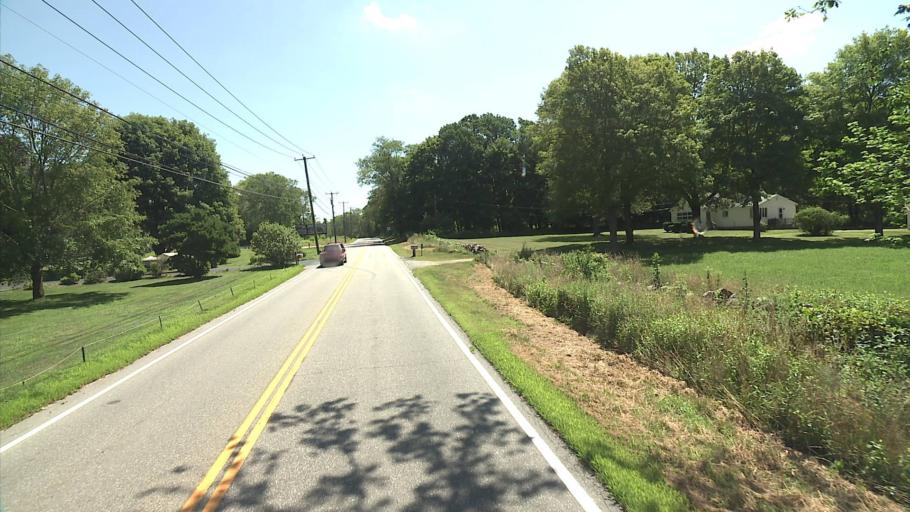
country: US
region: Connecticut
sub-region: Windham County
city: Moosup
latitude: 41.6910
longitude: -71.8369
